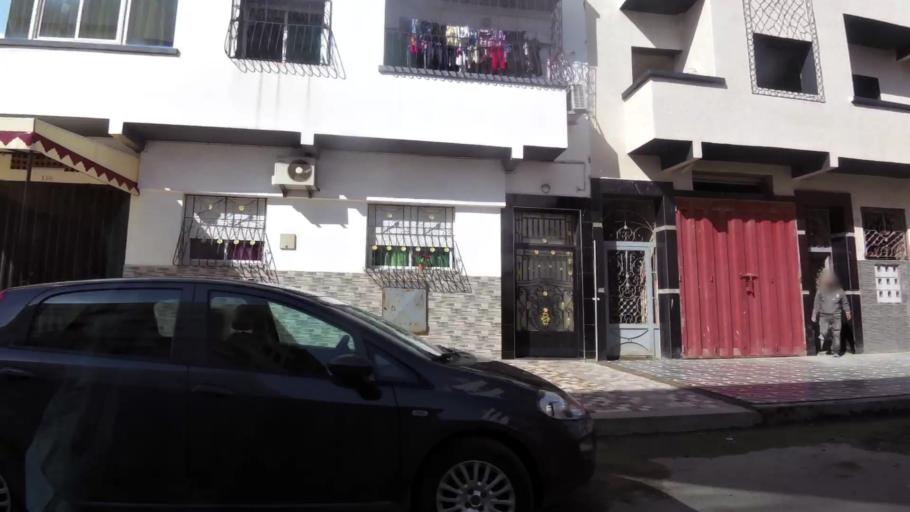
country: MA
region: Chaouia-Ouardigha
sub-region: Settat Province
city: Berrechid
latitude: 33.2586
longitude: -7.5761
